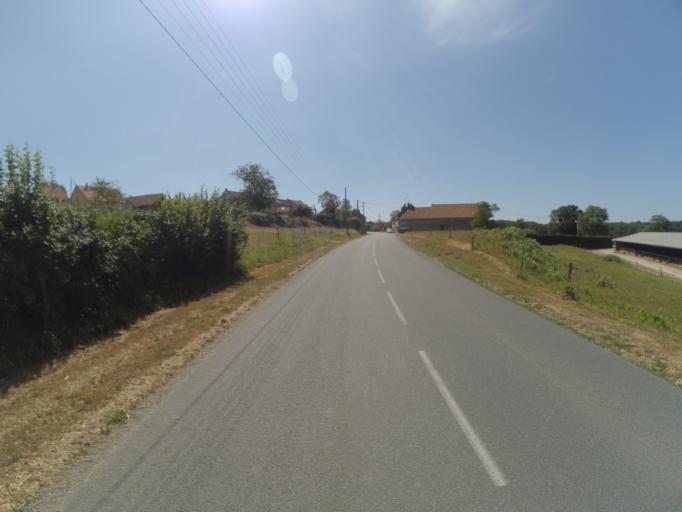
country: FR
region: Limousin
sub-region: Departement de la Creuse
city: Le Grand-Bourg
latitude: 46.0819
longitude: 1.6883
